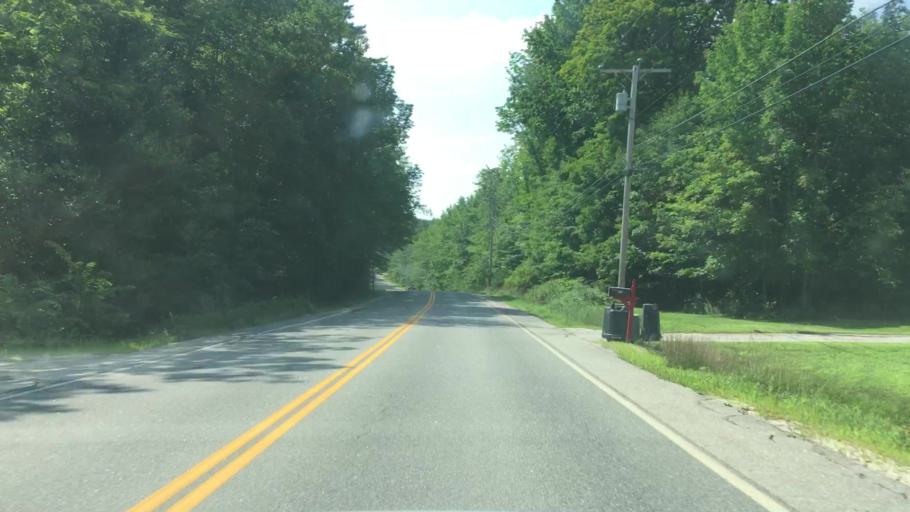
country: US
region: Maine
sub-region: Cumberland County
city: Raymond
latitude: 43.9276
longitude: -70.4368
